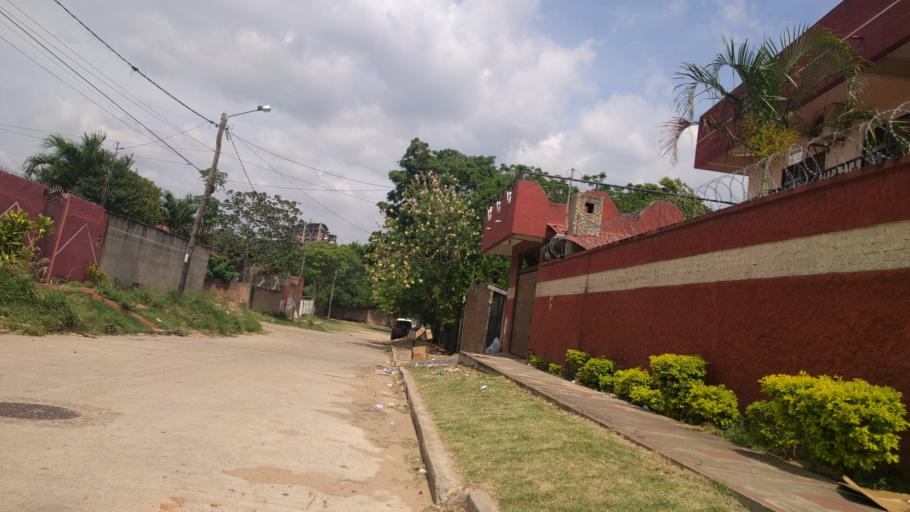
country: BO
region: Santa Cruz
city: Santa Cruz de la Sierra
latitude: -17.7915
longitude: -63.2196
